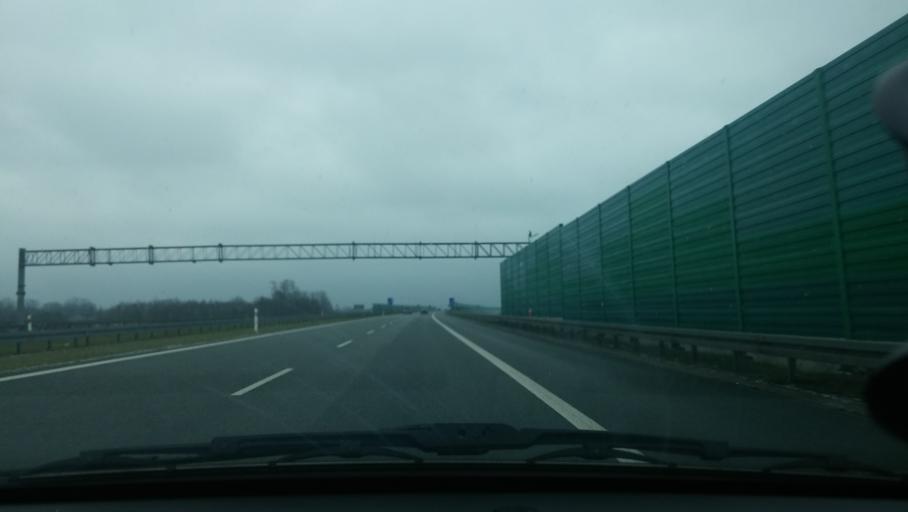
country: PL
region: Masovian Voivodeship
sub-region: Powiat minski
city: Kaluszyn
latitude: 52.2016
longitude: 21.7568
